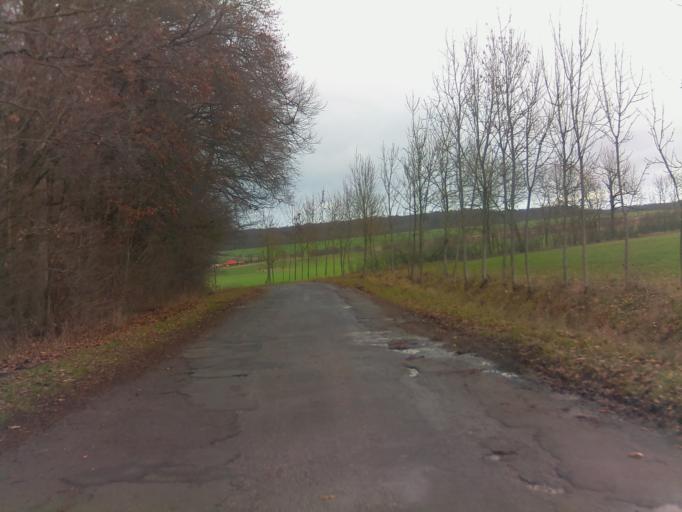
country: DE
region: Thuringia
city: Nauendorf
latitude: 50.9071
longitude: 11.1917
